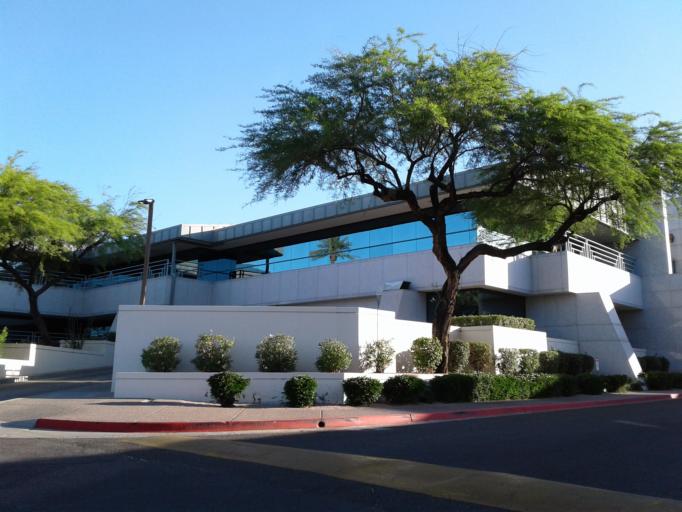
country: US
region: Arizona
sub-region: Maricopa County
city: Paradise Valley
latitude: 33.5244
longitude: -112.0286
